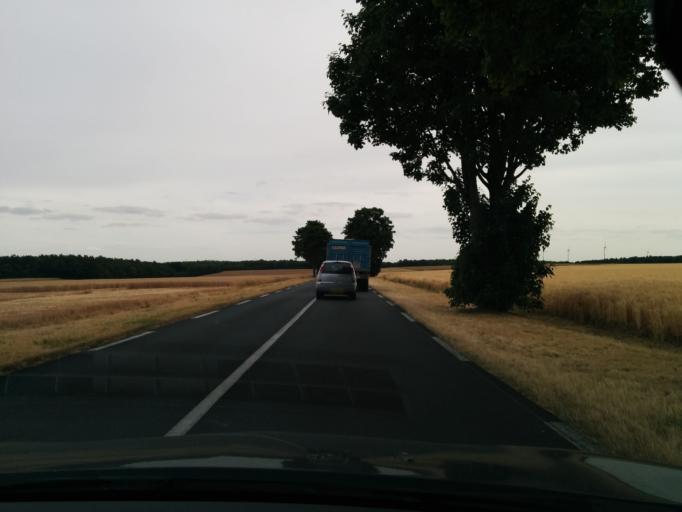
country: FR
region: Ile-de-France
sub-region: Departement de l'Essonne
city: Pussay
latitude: 48.3712
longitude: 1.9799
